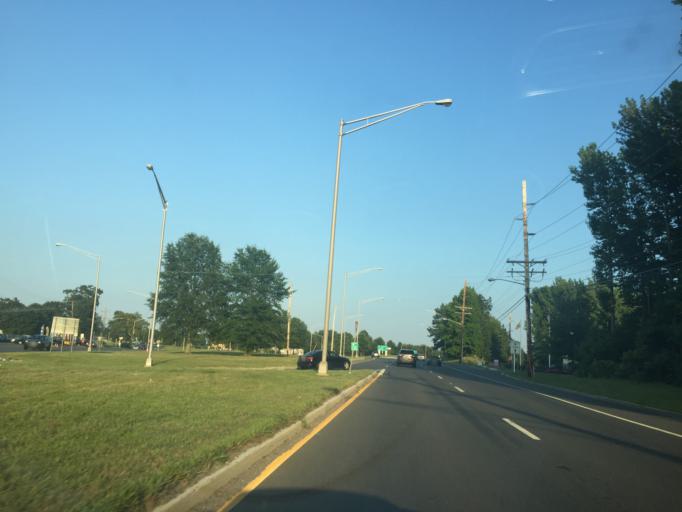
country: US
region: New Jersey
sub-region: Monmouth County
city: Shark River Hills
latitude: 40.2174
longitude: -74.1053
